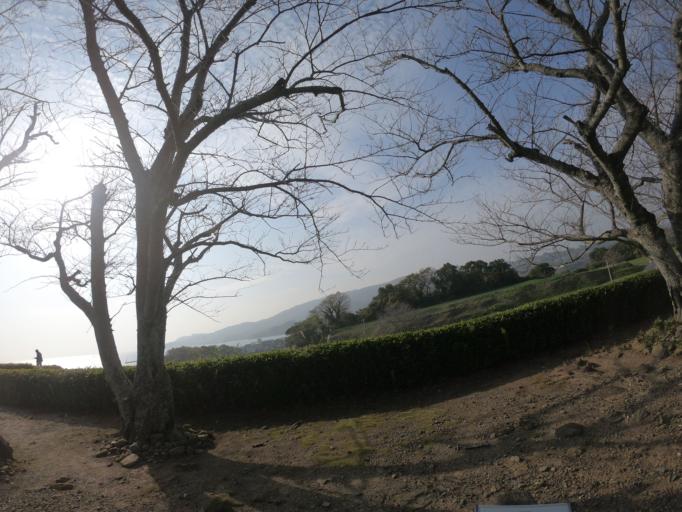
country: JP
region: Kumamoto
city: Hondo
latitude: 32.6292
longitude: 130.2540
